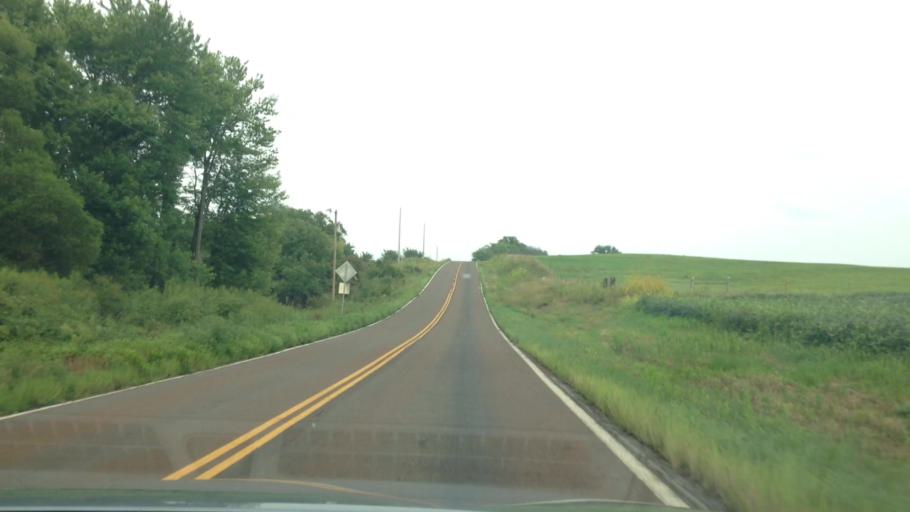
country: US
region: Missouri
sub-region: Clay County
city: Smithville
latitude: 39.4050
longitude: -94.6537
